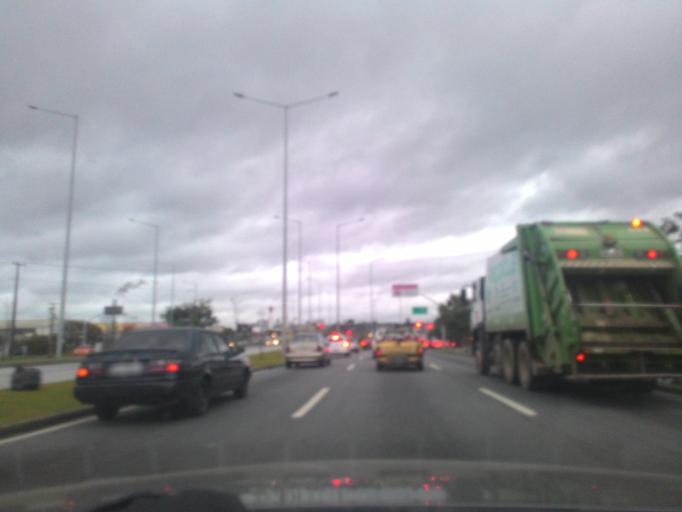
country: BR
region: Parana
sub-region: Curitiba
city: Curitiba
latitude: -25.4770
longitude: -49.2600
